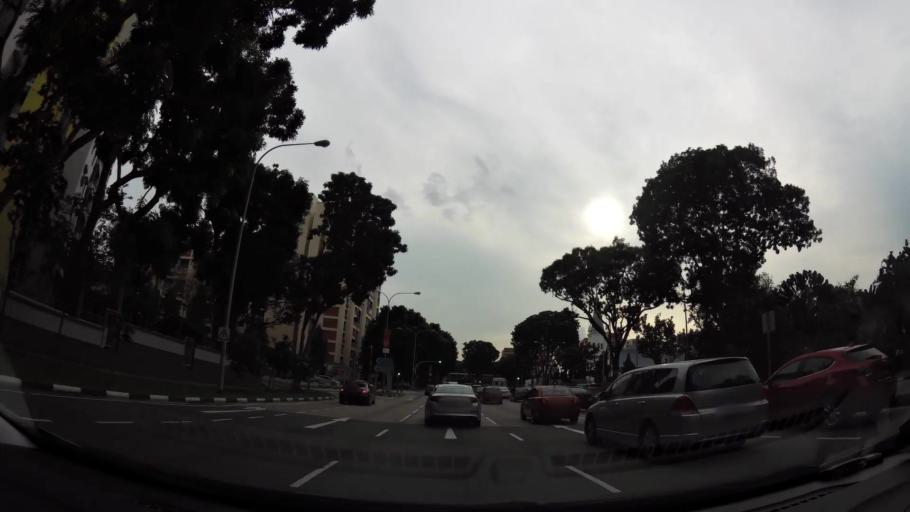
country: SG
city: Singapore
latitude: 1.3740
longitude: 103.8999
